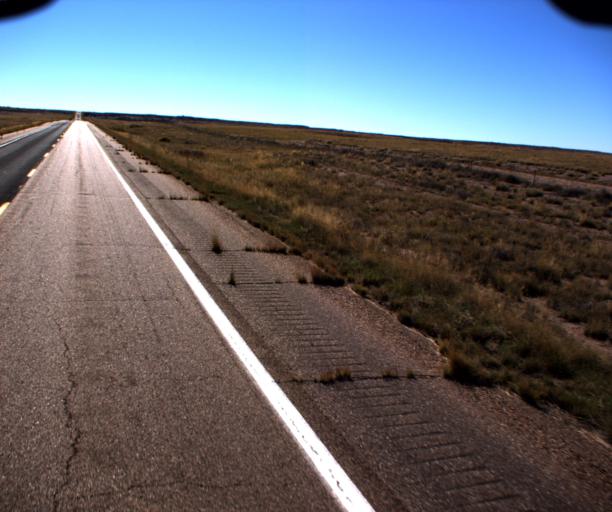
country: US
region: Arizona
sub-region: Navajo County
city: Snowflake
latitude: 34.7303
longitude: -109.7820
